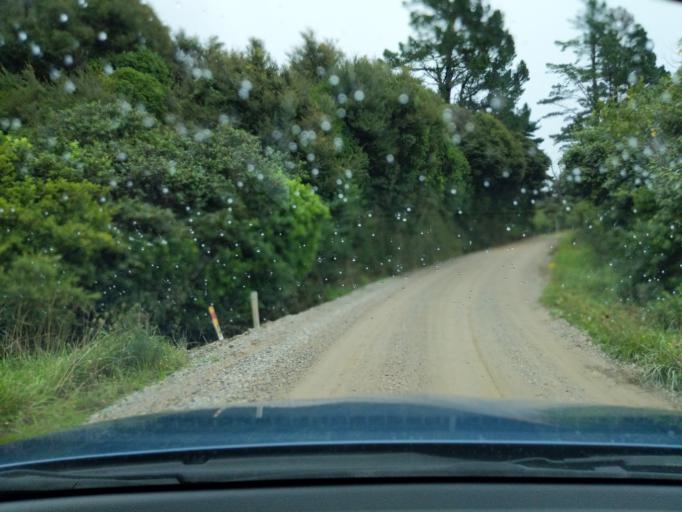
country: NZ
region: Tasman
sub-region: Tasman District
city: Takaka
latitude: -40.6307
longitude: 172.5112
